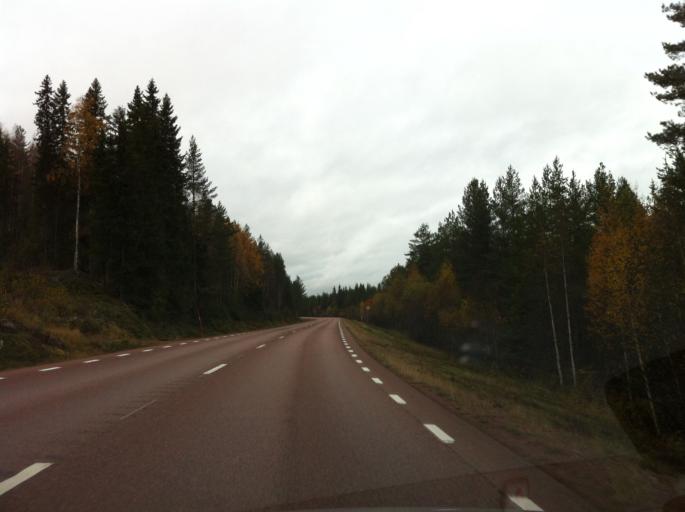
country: SE
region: Dalarna
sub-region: Alvdalens Kommun
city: AElvdalen
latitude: 61.2727
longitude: 13.7908
